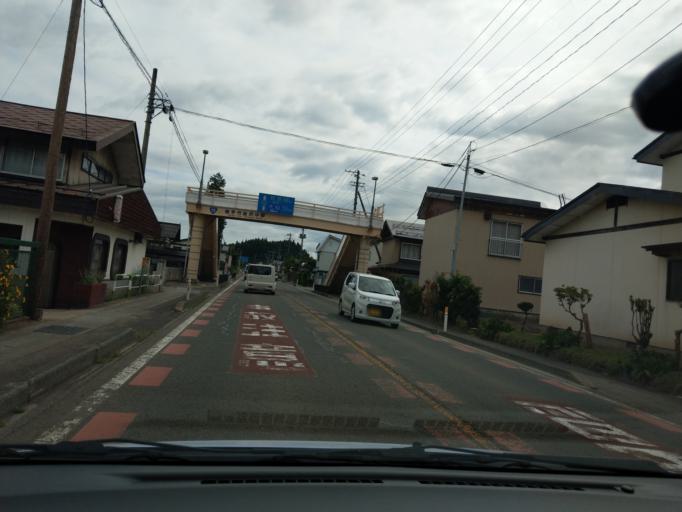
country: JP
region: Akita
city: Yokotemachi
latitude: 39.3690
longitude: 140.5680
